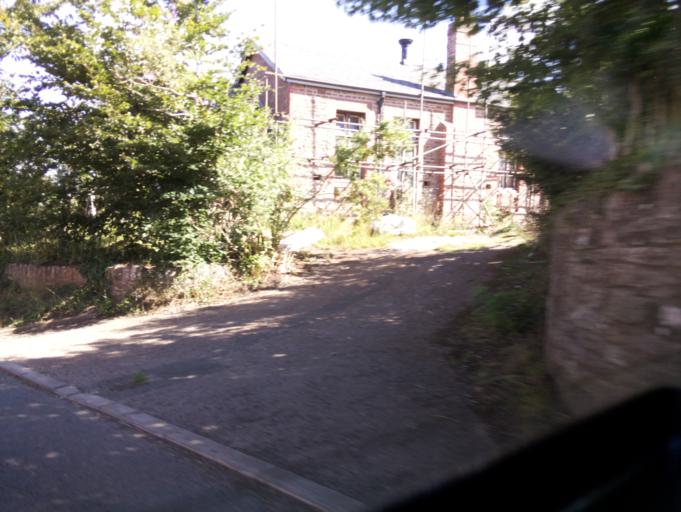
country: GB
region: England
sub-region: Herefordshire
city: Linton
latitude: 51.9399
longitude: -2.5258
